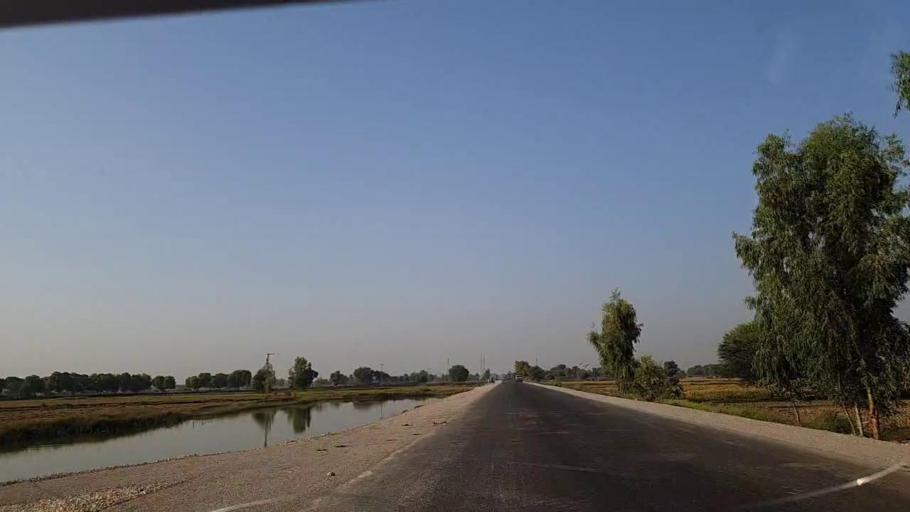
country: PK
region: Sindh
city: Rustam jo Goth
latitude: 27.9522
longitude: 68.8088
